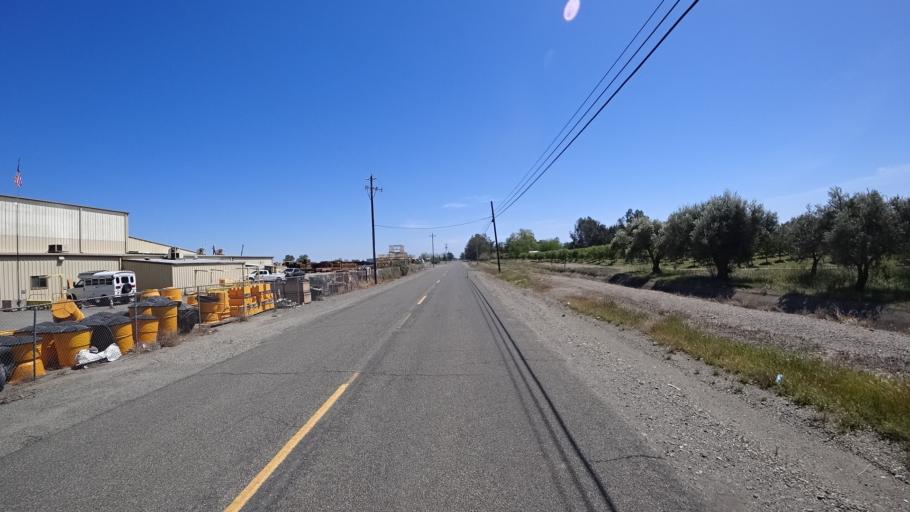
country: US
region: California
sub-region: Glenn County
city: Orland
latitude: 39.7350
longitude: -122.1657
